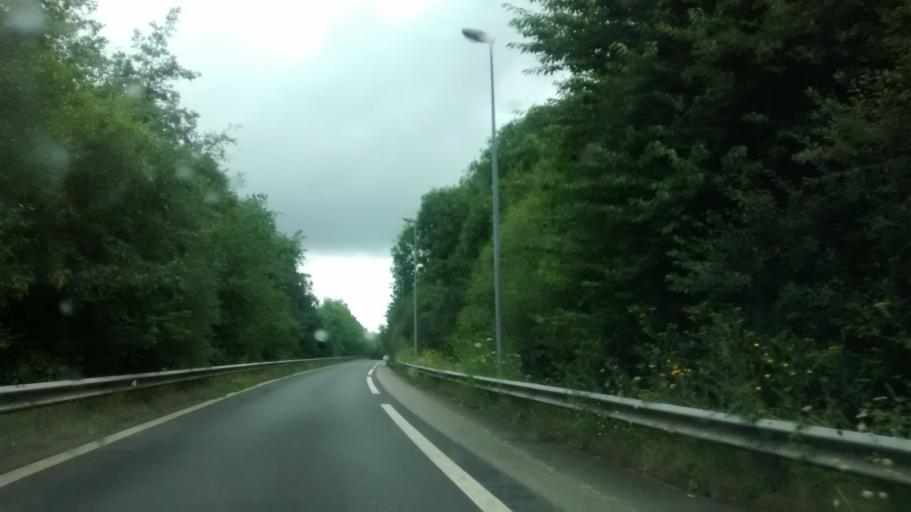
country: FR
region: Haute-Normandie
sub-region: Departement de la Seine-Maritime
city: Bois-Guillaume
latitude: 49.4645
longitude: 1.1369
